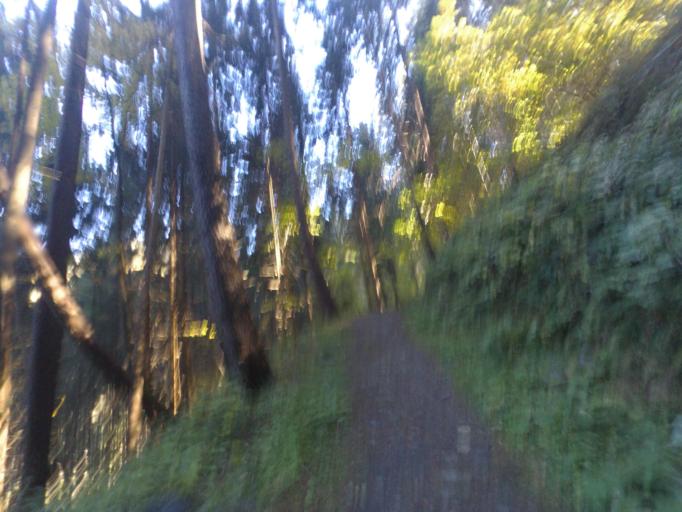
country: AT
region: Salzburg
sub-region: Politischer Bezirk Sankt Johann im Pongau
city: Sankt Johann im Pongau
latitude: 47.3172
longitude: 13.1890
